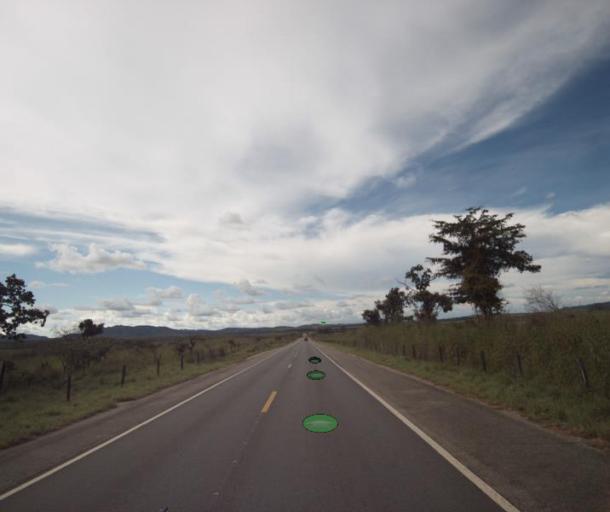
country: BR
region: Goias
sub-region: Barro Alto
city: Barro Alto
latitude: -15.1873
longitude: -48.7033
